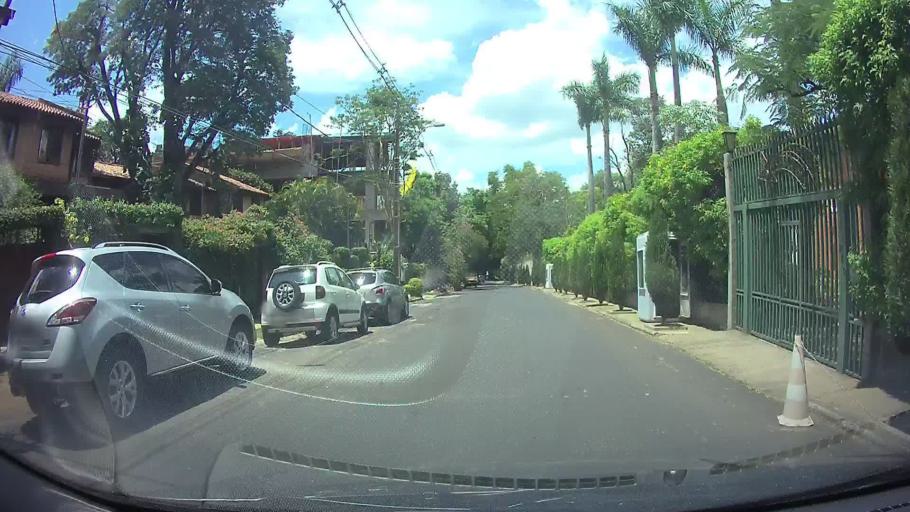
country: PY
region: Asuncion
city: Asuncion
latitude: -25.2964
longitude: -57.6063
